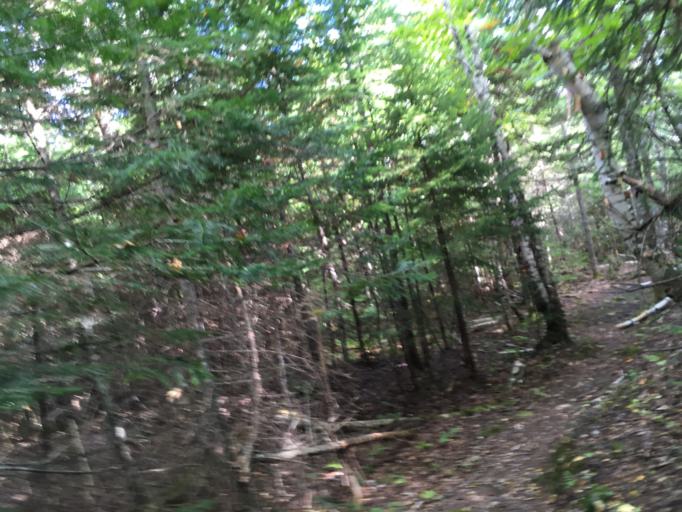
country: US
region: Maine
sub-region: Penobscot County
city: Millinocket
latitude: 45.9206
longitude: -68.8552
